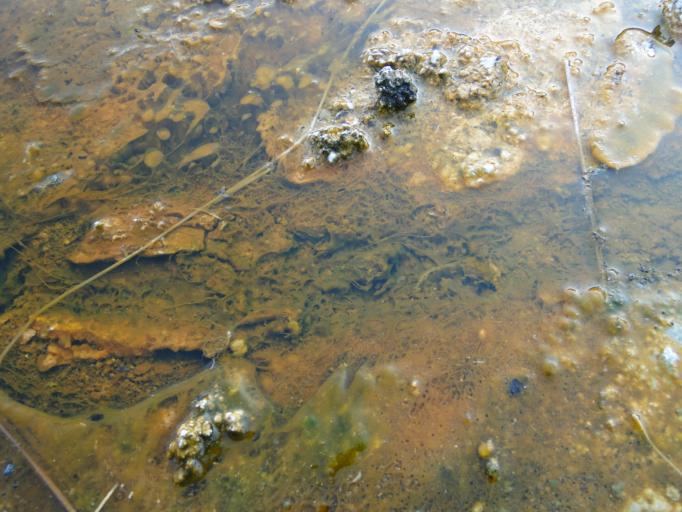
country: US
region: Montana
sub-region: Gallatin County
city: West Yellowstone
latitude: 44.5163
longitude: -110.8329
